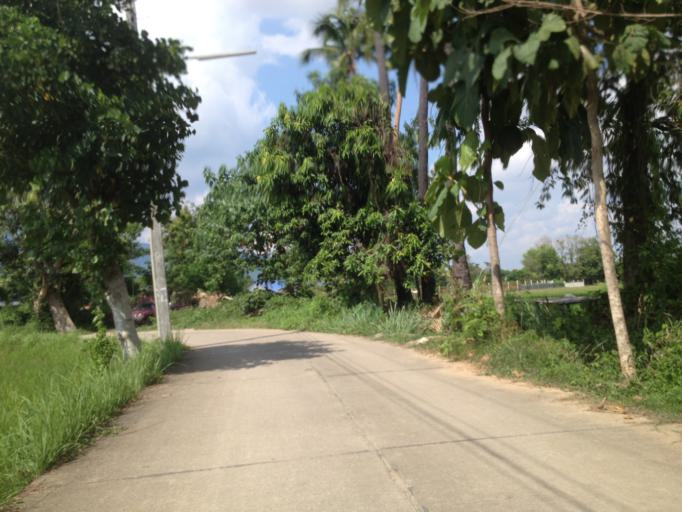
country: TH
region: Chiang Mai
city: Hang Dong
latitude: 18.7286
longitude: 98.9205
